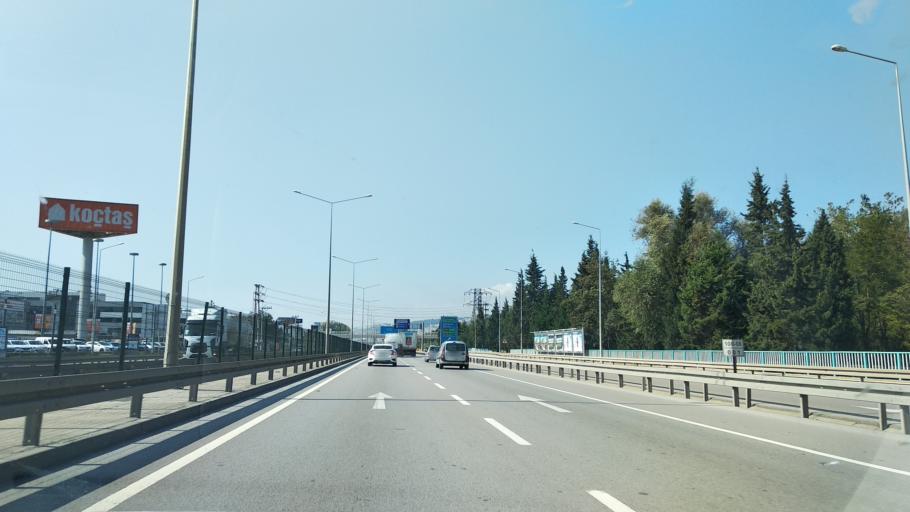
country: TR
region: Kocaeli
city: Kullar
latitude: 40.7599
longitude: 29.9786
